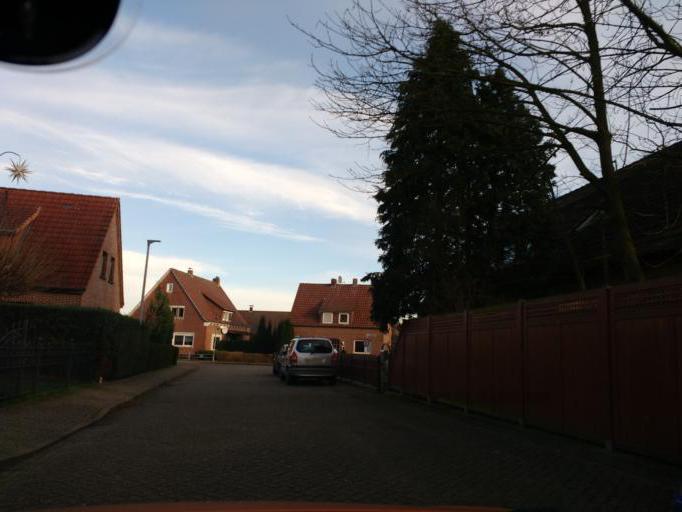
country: DE
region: Lower Saxony
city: Hude
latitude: 53.1155
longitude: 8.4561
